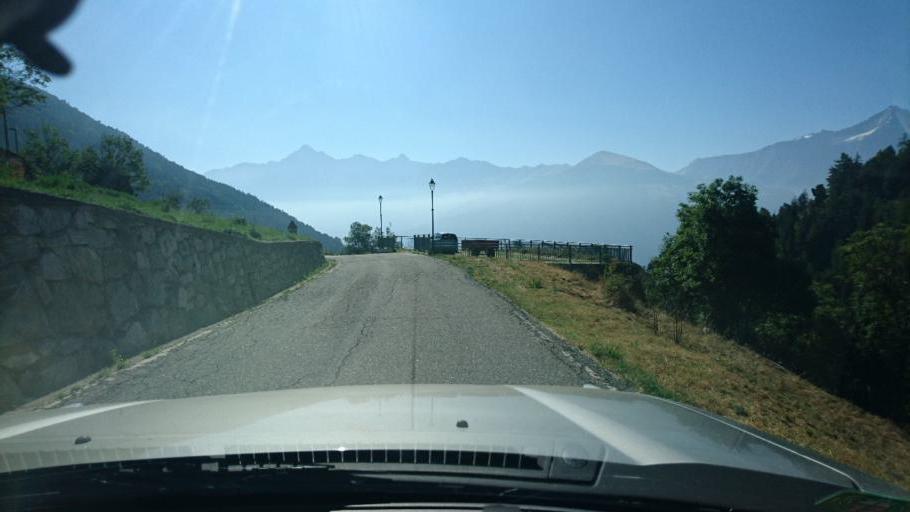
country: IT
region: Aosta Valley
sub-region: Valle d'Aosta
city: Saint-Pierre
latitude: 45.7354
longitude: 7.2063
